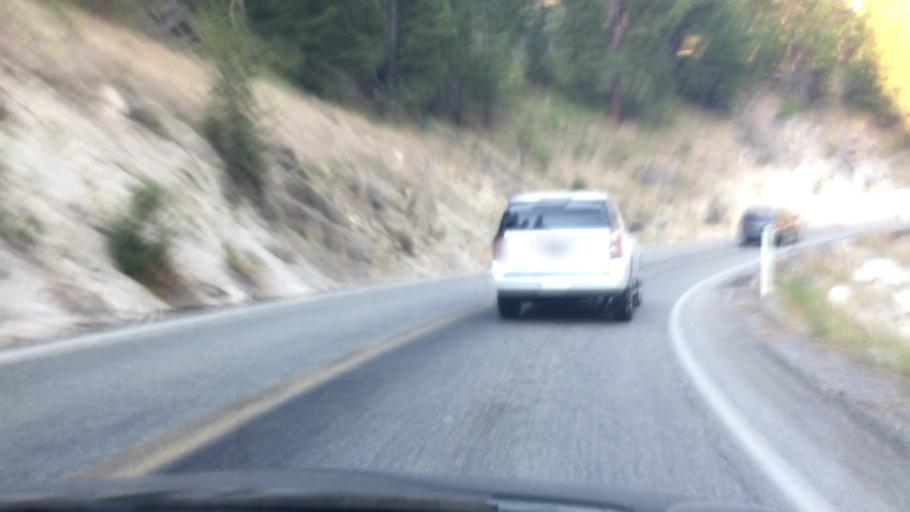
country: US
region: Idaho
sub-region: Valley County
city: Cascade
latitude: 44.3177
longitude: -116.0671
